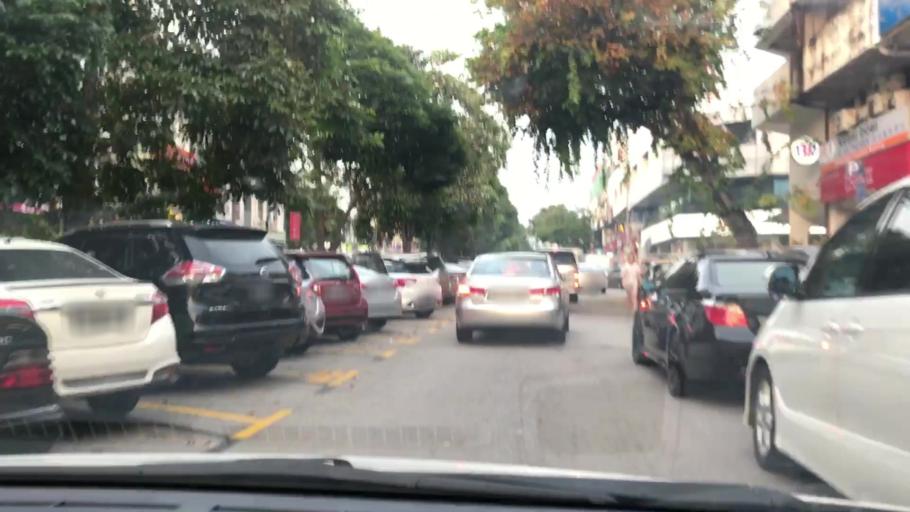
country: MY
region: Selangor
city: Kampong Baharu Balakong
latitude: 3.0685
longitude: 101.6917
